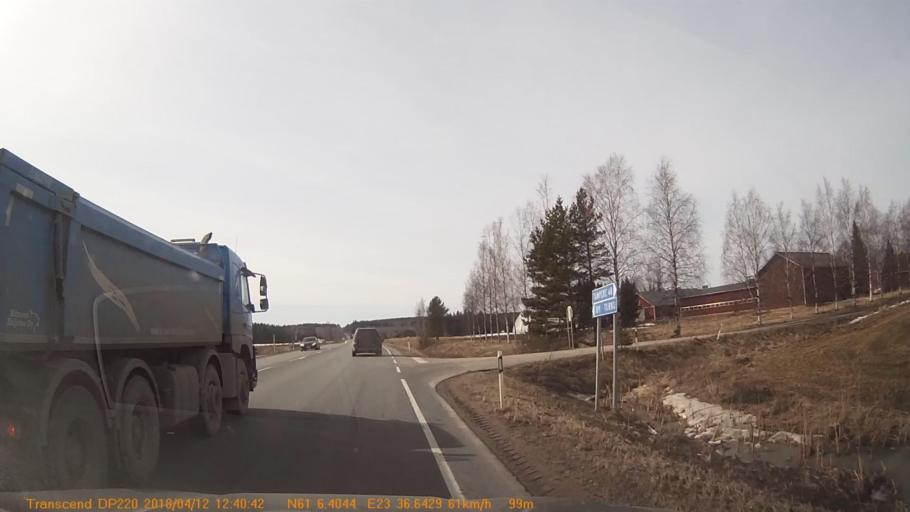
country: FI
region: Pirkanmaa
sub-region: Etelae-Pirkanmaa
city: Urjala
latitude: 61.1067
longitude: 23.6104
